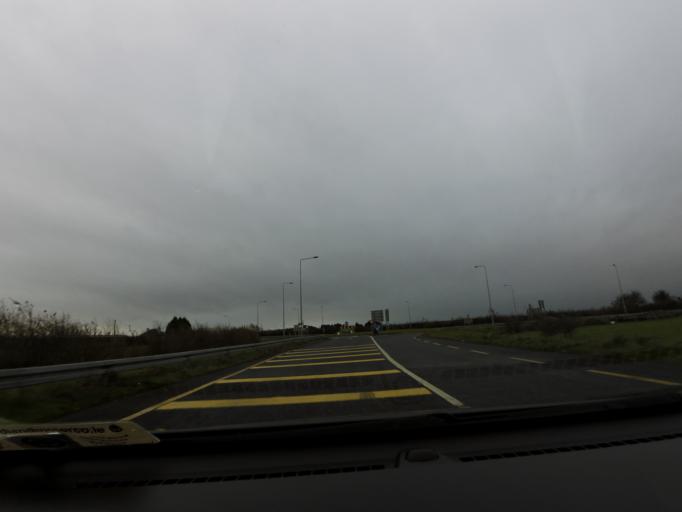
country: IE
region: Connaught
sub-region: County Galway
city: Loughrea
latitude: 53.2044
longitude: -8.5425
